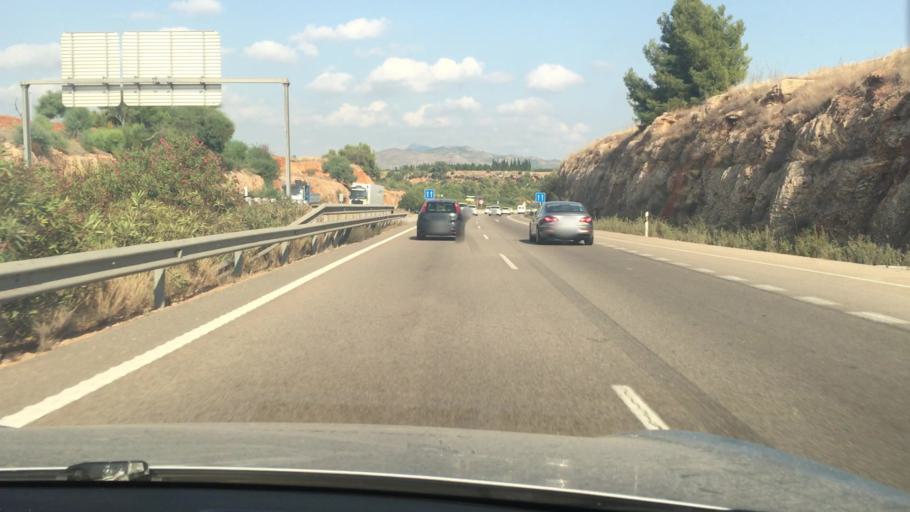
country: ES
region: Valencia
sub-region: Provincia de Castello
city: Vila-real
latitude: 39.9808
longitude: -0.1414
